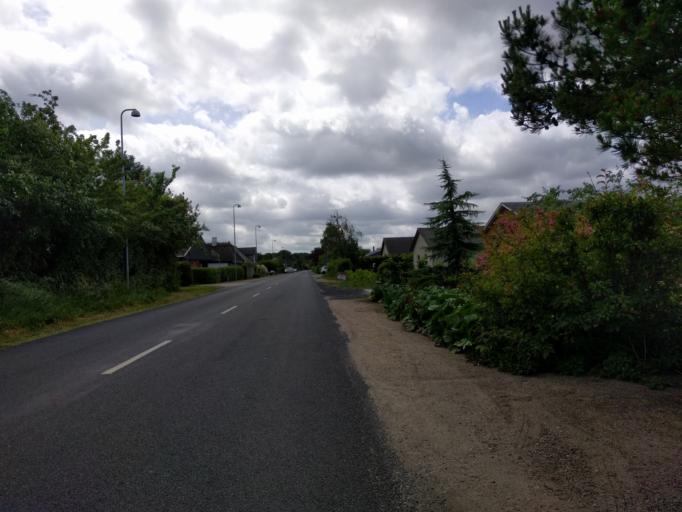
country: DK
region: South Denmark
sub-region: Odense Kommune
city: Bullerup
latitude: 55.4328
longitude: 10.4881
